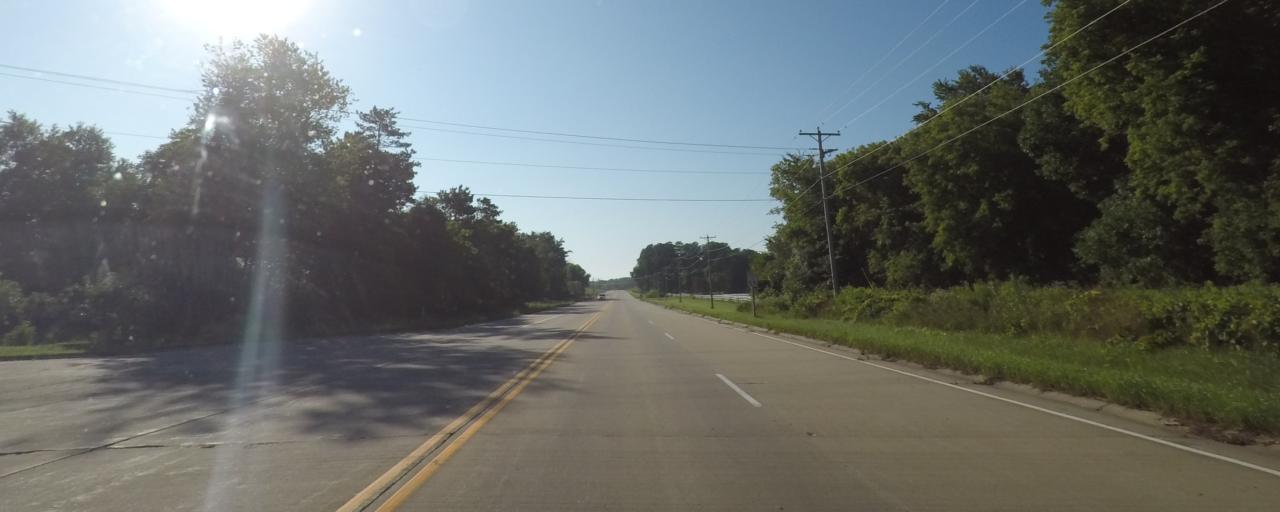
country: US
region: Wisconsin
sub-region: Jefferson County
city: Lake Ripley
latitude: 42.9906
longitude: -88.9954
